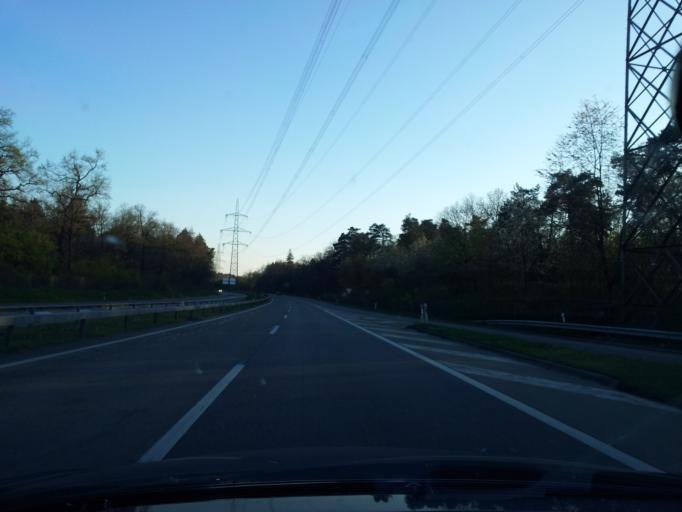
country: CH
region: Bern
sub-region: Seeland District
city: Lyss
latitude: 47.0802
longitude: 7.2924
